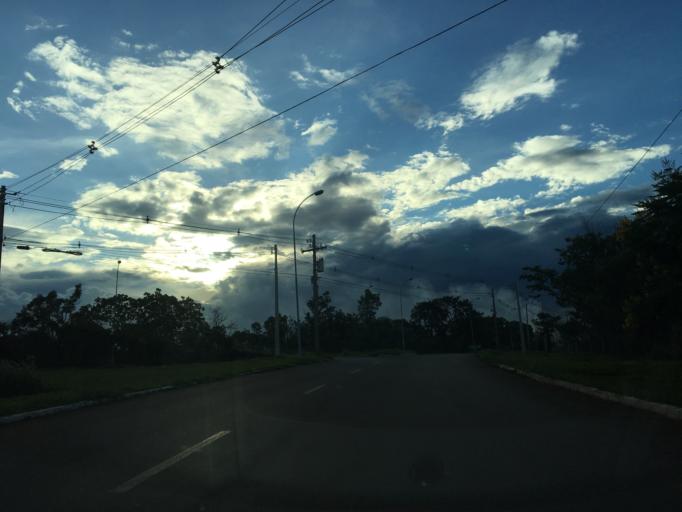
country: BR
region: Federal District
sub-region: Brasilia
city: Brasilia
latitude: -15.8065
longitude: -47.8386
